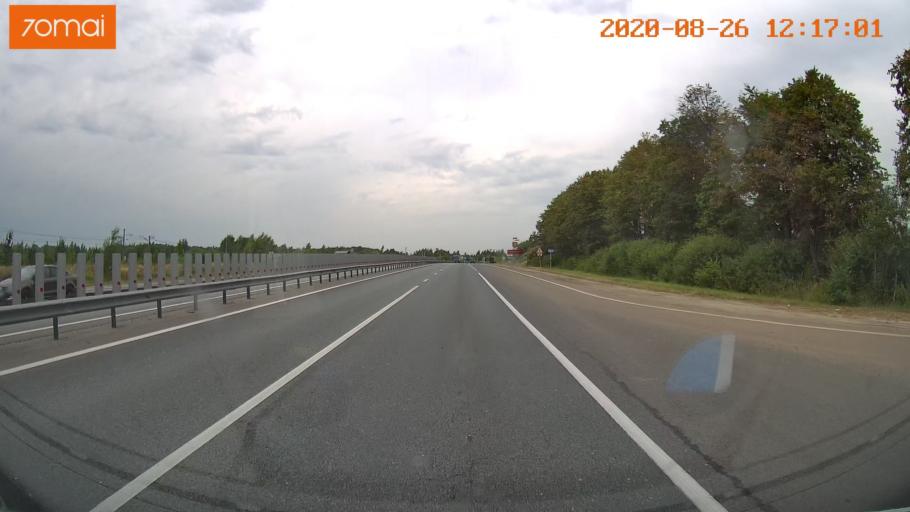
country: RU
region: Rjazan
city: Murmino
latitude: 54.4549
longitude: 40.0334
